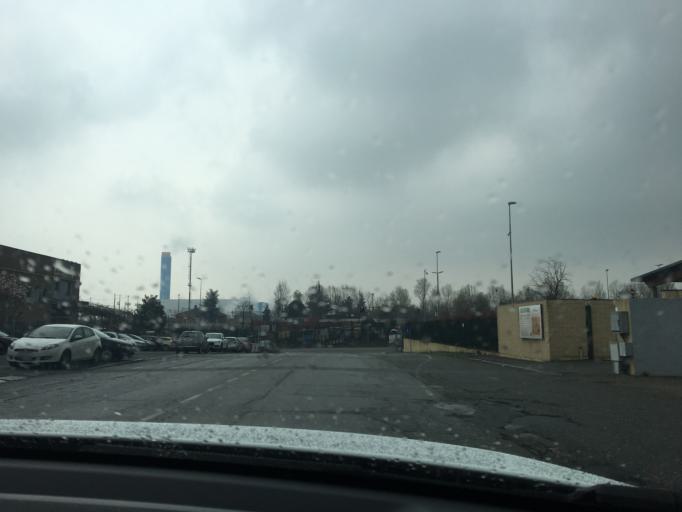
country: IT
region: Piedmont
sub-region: Provincia di Torino
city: Grugliasco
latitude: 45.0449
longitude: 7.5894
